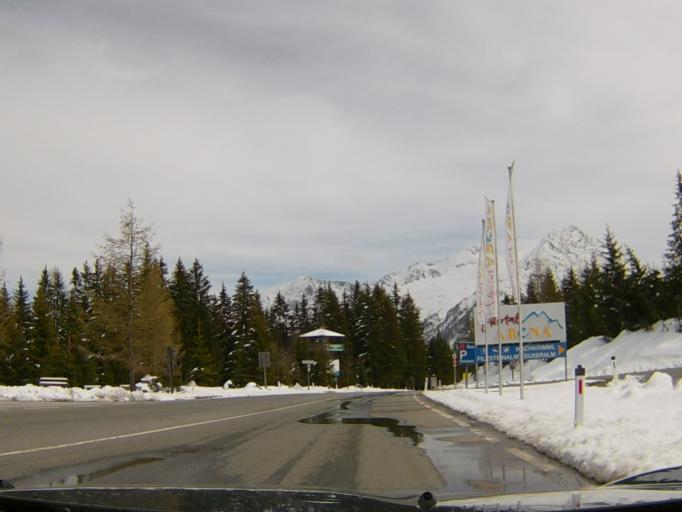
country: AT
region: Salzburg
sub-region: Politischer Bezirk Zell am See
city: Krimml
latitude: 47.2365
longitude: 12.1588
